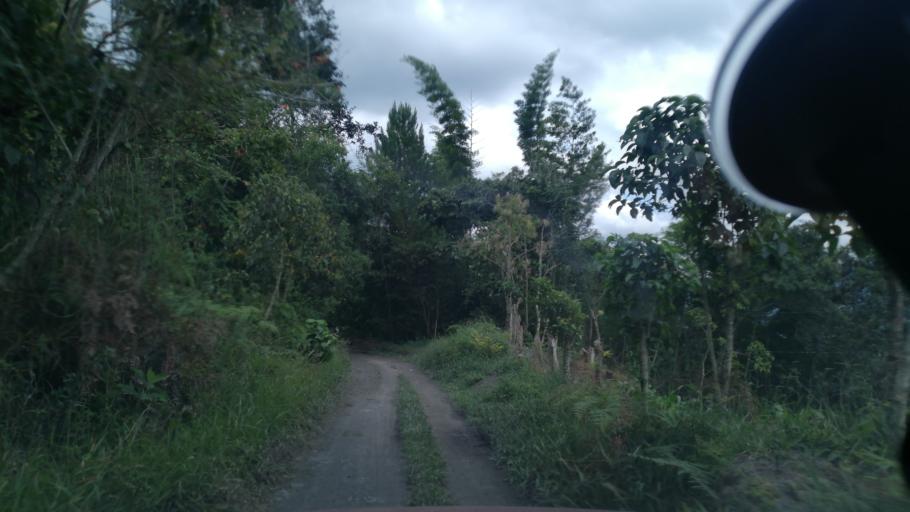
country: CO
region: Cundinamarca
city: Vergara
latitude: 5.2088
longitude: -74.2858
